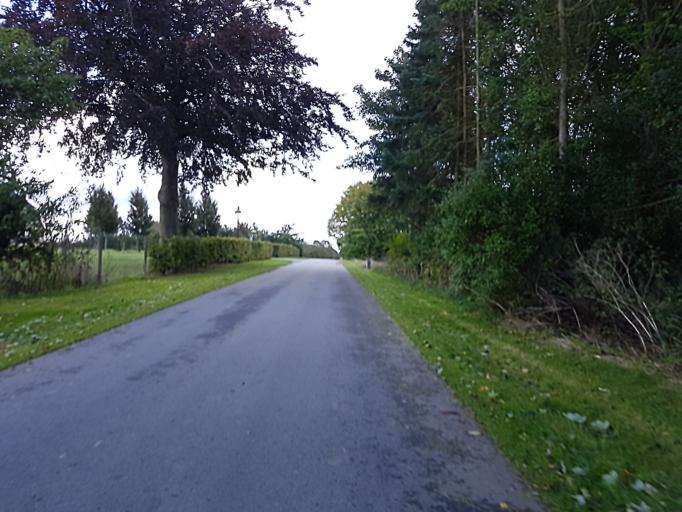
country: DK
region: Zealand
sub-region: Roskilde Kommune
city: Gundsomagle
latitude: 55.7214
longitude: 12.1760
